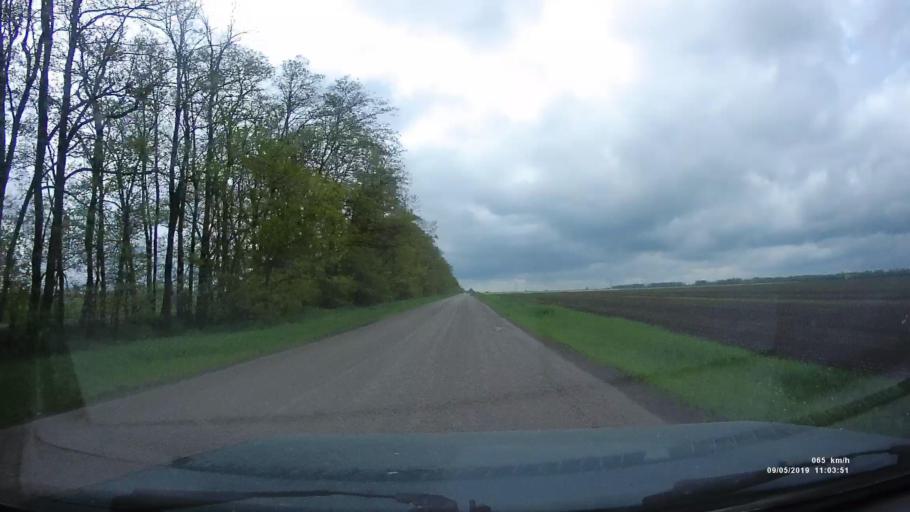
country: RU
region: Krasnodarskiy
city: Kanelovskaya
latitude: 46.8238
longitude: 39.2101
